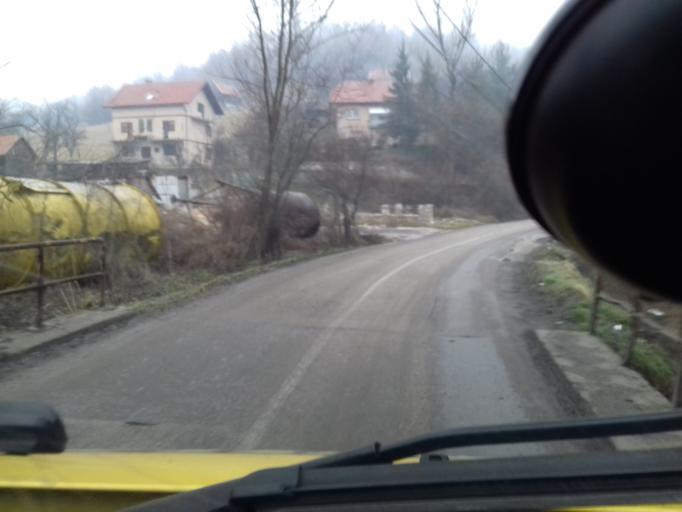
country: BA
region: Federation of Bosnia and Herzegovina
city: Lokvine
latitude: 44.2074
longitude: 17.8558
